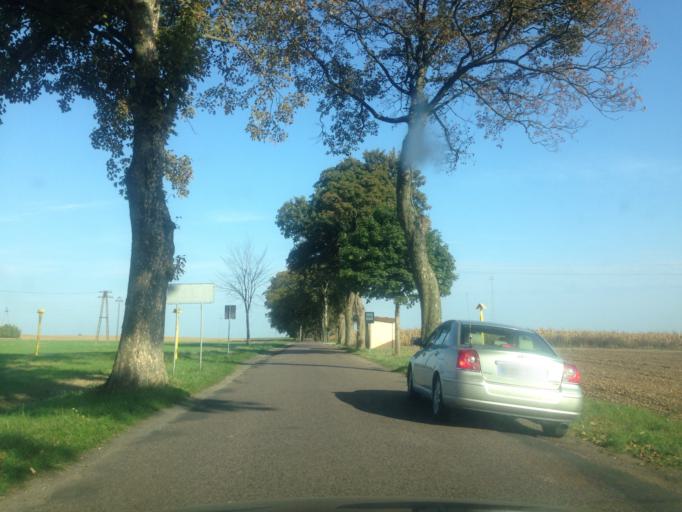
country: PL
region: Kujawsko-Pomorskie
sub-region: Powiat brodnicki
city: Brzozie
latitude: 53.3284
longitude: 19.5496
